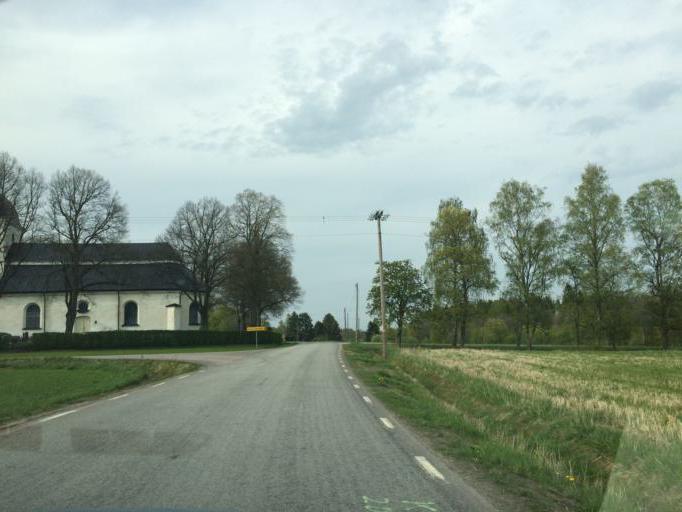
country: SE
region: Vaestmanland
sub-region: Kopings Kommun
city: Koping
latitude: 59.5827
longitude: 15.9860
